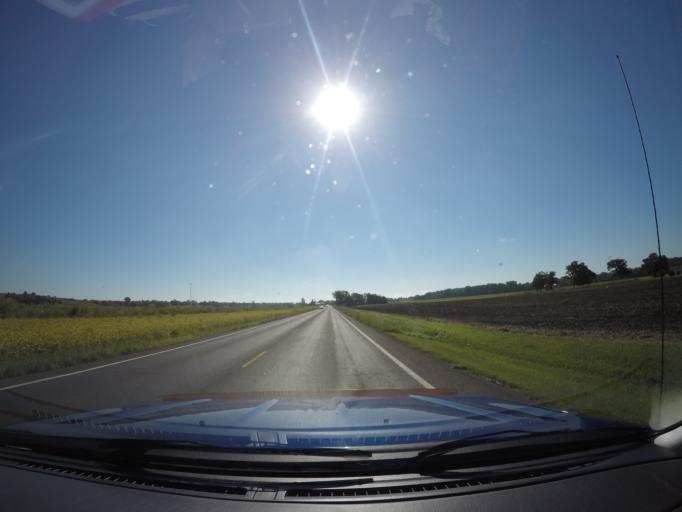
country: US
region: Kansas
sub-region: Pottawatomie County
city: Saint Marys
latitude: 39.2023
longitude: -96.0913
